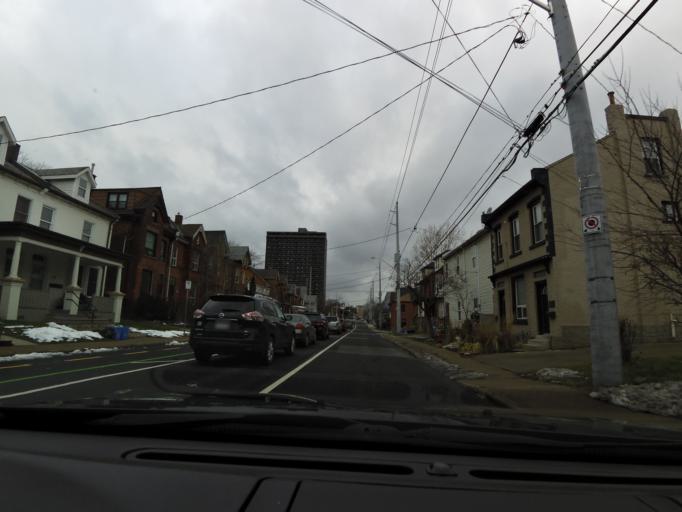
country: CA
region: Ontario
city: Hamilton
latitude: 43.2511
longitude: -79.8608
